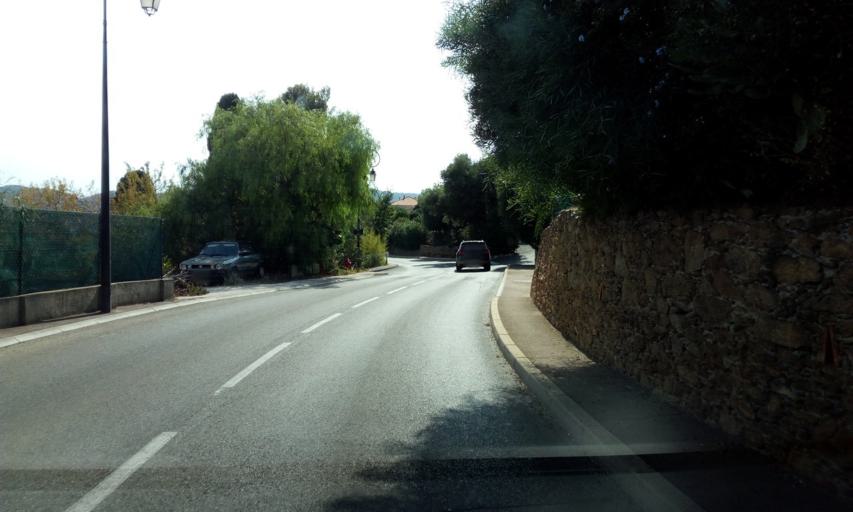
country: FR
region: Provence-Alpes-Cote d'Azur
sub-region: Departement du Var
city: Bormes-les-Mimosas
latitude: 43.1469
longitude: 6.3406
